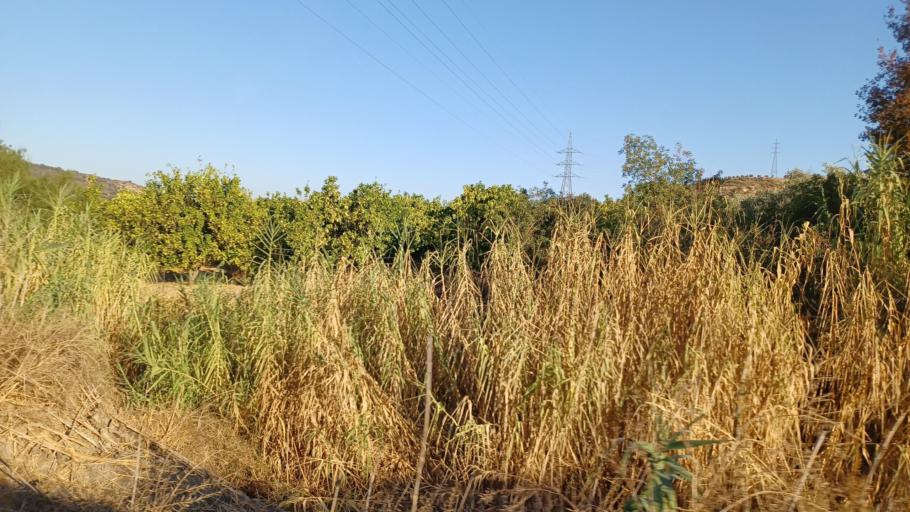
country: CY
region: Pafos
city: Polis
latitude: 34.9789
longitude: 32.4583
